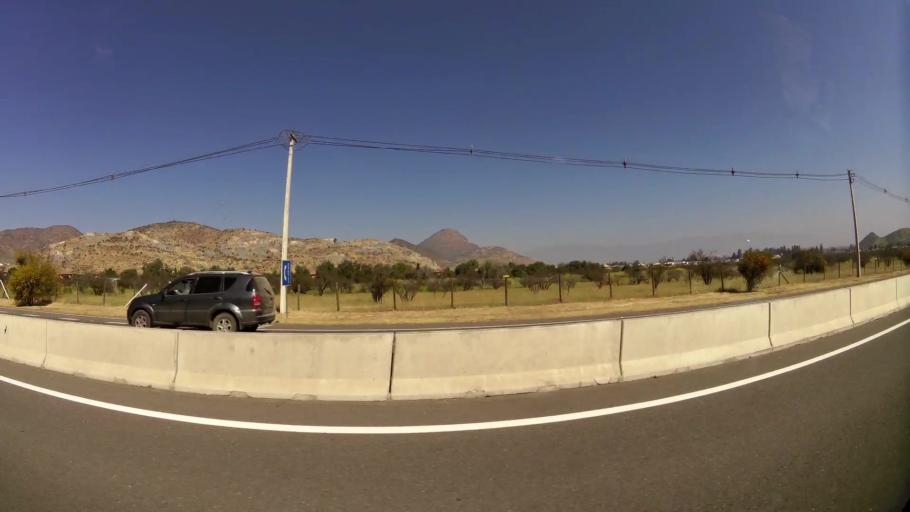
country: CL
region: Santiago Metropolitan
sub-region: Provincia de Chacabuco
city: Chicureo Abajo
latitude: -33.3065
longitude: -70.6543
